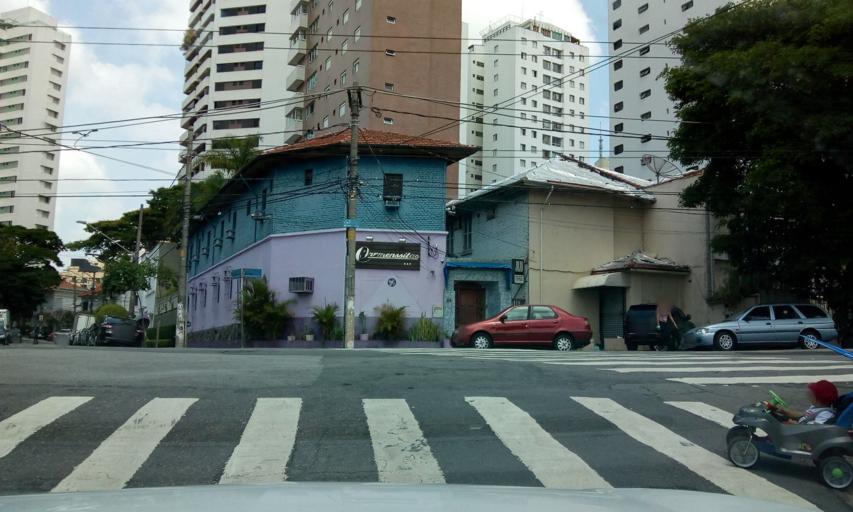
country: BR
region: Sao Paulo
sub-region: Sao Paulo
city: Sao Paulo
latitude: -23.5703
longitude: -46.6316
